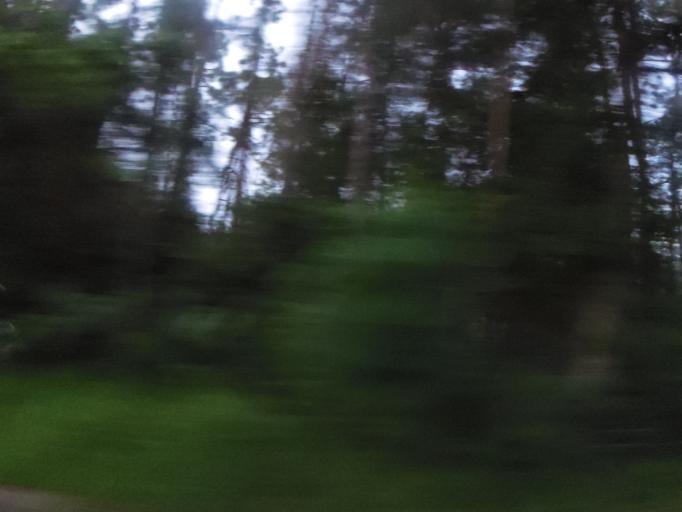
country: US
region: Florida
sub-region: Duval County
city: Jacksonville
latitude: 30.2421
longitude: -81.6107
